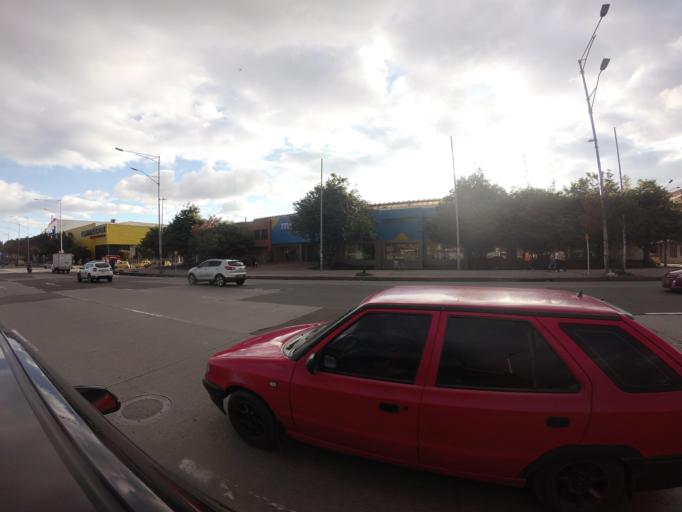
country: CO
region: Cundinamarca
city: Cota
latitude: 4.7570
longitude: -74.0462
